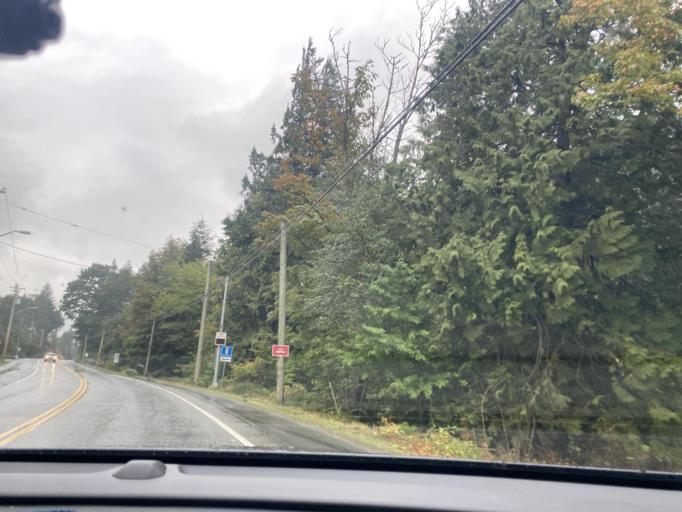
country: CA
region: British Columbia
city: Agassiz
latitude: 49.3001
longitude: -121.7854
